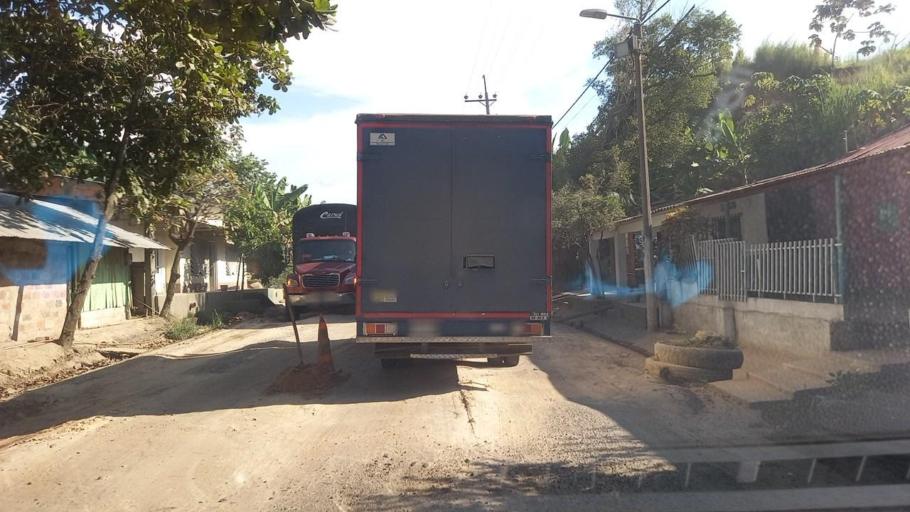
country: CO
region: Boyaca
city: Puerto Boyaca
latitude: 5.9352
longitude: -74.5697
